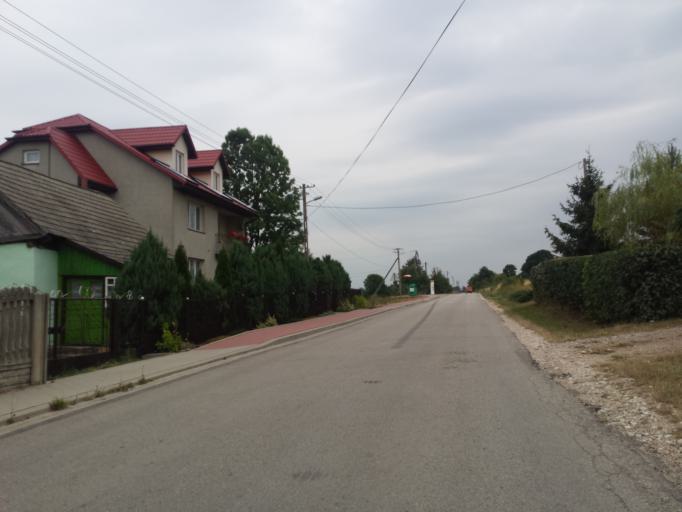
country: PL
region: Swietokrzyskie
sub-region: Powiat kielecki
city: Morawica
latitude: 50.7312
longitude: 20.6827
